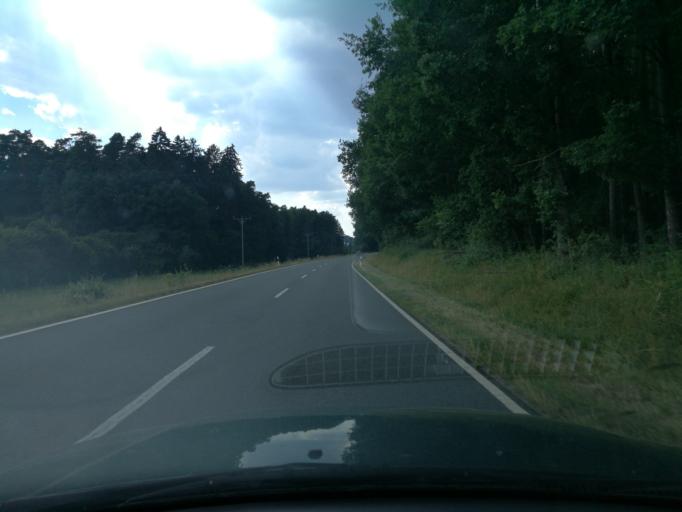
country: DE
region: Bavaria
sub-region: Regierungsbezirk Mittelfranken
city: Grosshabersdorf
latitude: 49.4126
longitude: 10.7536
